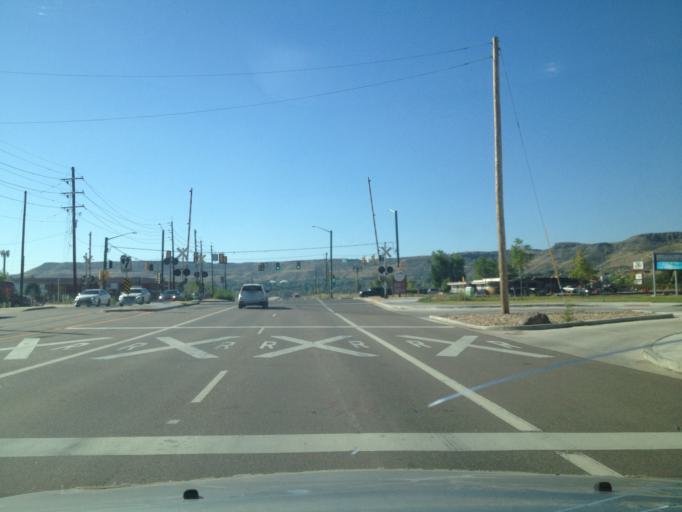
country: US
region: Colorado
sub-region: Jefferson County
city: Applewood
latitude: 39.7771
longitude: -105.1749
